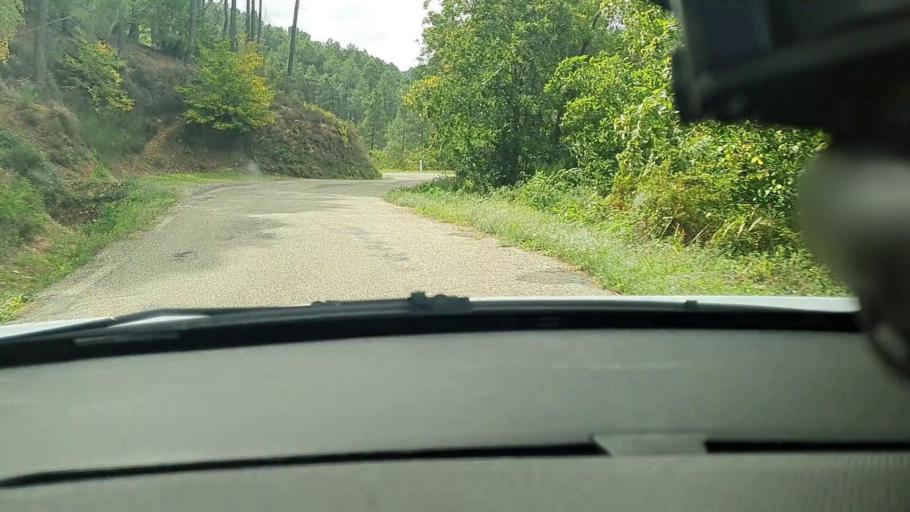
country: FR
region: Languedoc-Roussillon
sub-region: Departement du Gard
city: Branoux-les-Taillades
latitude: 44.2744
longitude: 3.9757
